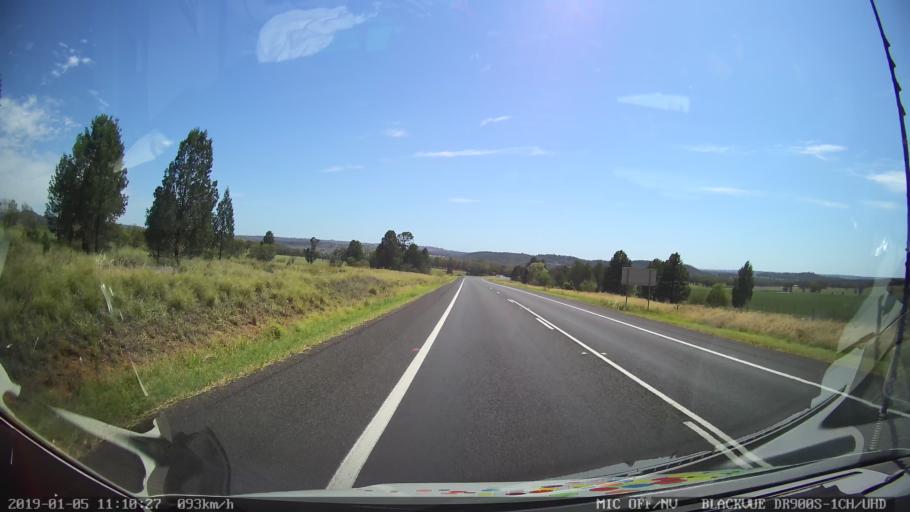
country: AU
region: New South Wales
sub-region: Warrumbungle Shire
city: Coonabarabran
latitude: -31.4063
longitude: 149.2444
